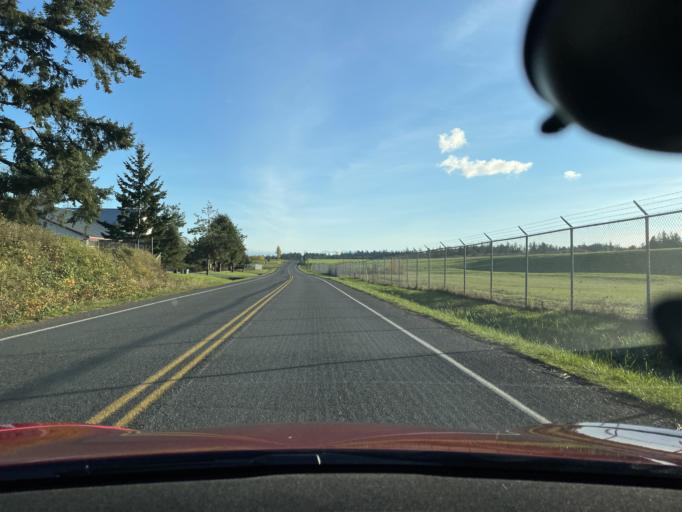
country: US
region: Washington
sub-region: San Juan County
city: Friday Harbor
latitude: 48.5239
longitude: -123.0232
